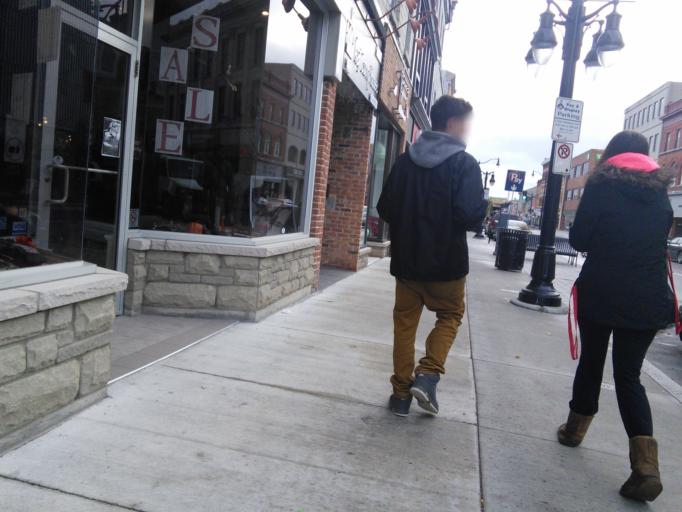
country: CA
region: Ontario
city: Kingston
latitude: 44.2317
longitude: -76.4837
